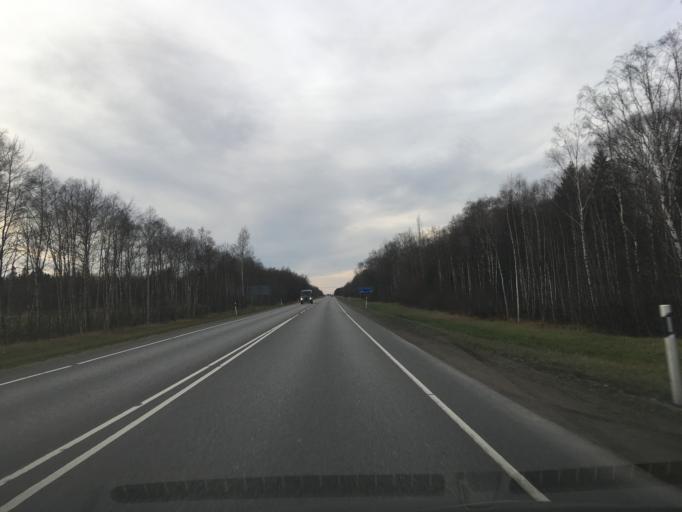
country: EE
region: Ida-Virumaa
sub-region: Kohtla-Jaerve linn
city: Kohtla-Jarve
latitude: 59.4209
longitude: 27.2700
